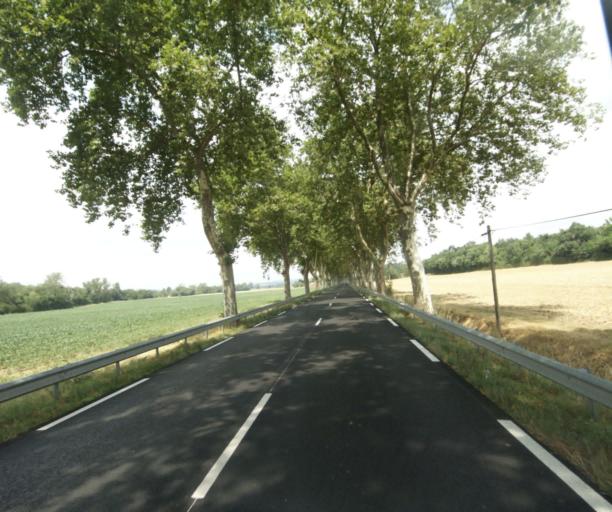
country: FR
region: Midi-Pyrenees
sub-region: Departement de la Haute-Garonne
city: Revel
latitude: 43.4364
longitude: 1.9528
